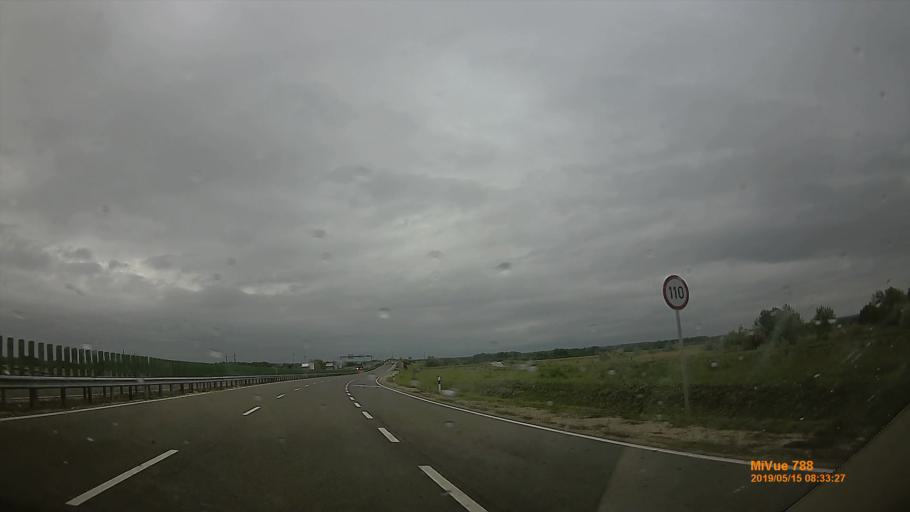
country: HU
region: Fejer
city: Szekesfehervar
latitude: 47.1788
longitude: 18.3803
